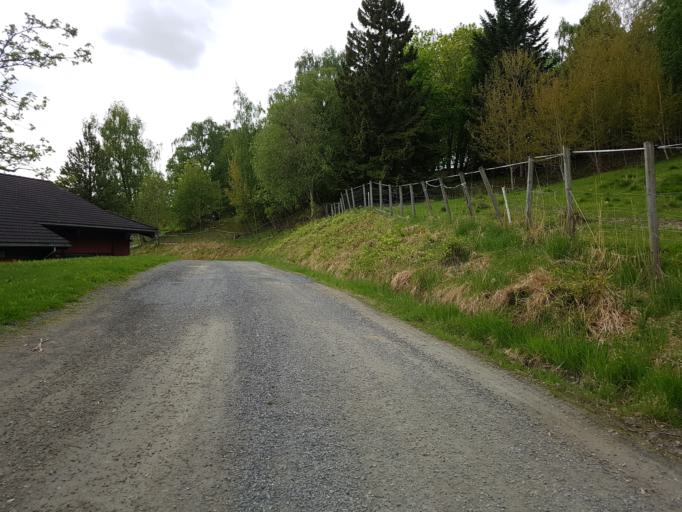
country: NO
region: Nord-Trondelag
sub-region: Levanger
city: Levanger
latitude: 63.7460
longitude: 11.2747
